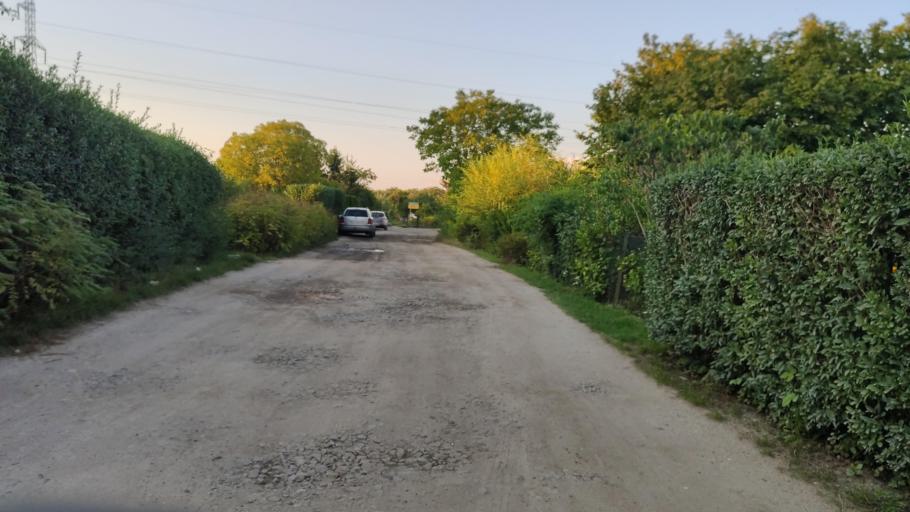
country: PL
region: Lower Silesian Voivodeship
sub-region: Powiat wroclawski
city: Wroclaw
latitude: 51.1009
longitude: 16.9799
